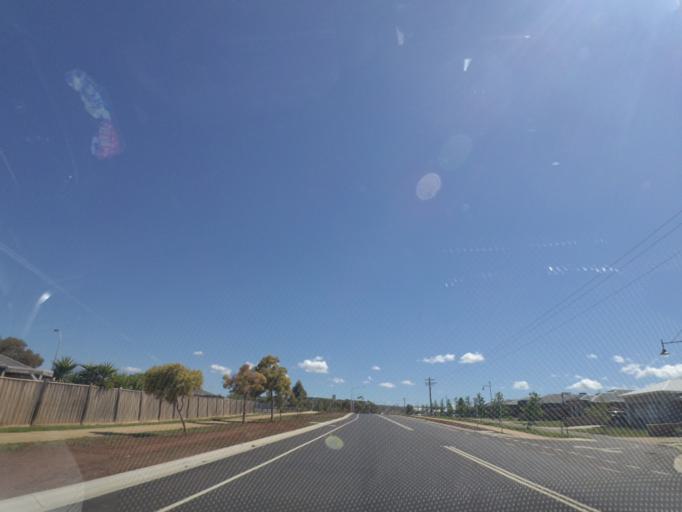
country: AU
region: Victoria
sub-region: Moorabool
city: Bacchus Marsh
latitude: -37.6883
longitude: 144.4156
